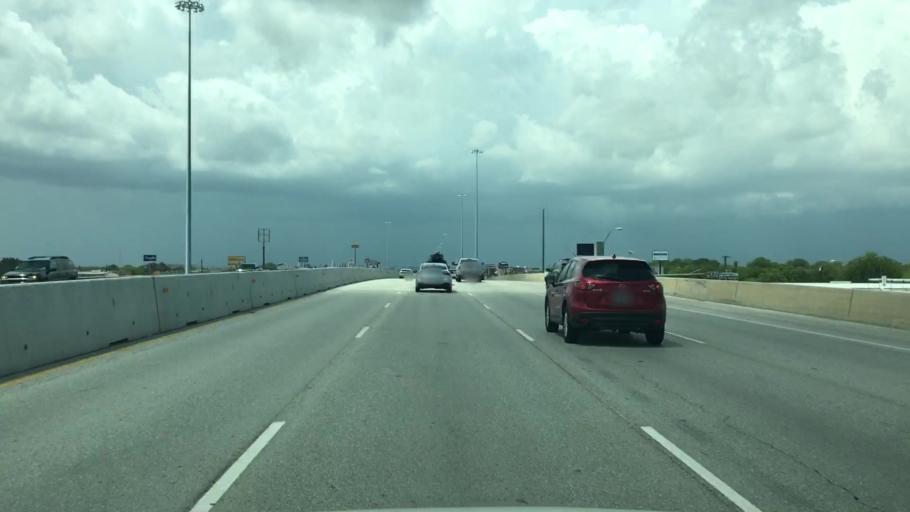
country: US
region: Texas
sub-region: Nueces County
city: Corpus Christi
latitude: 27.7249
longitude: -97.4052
